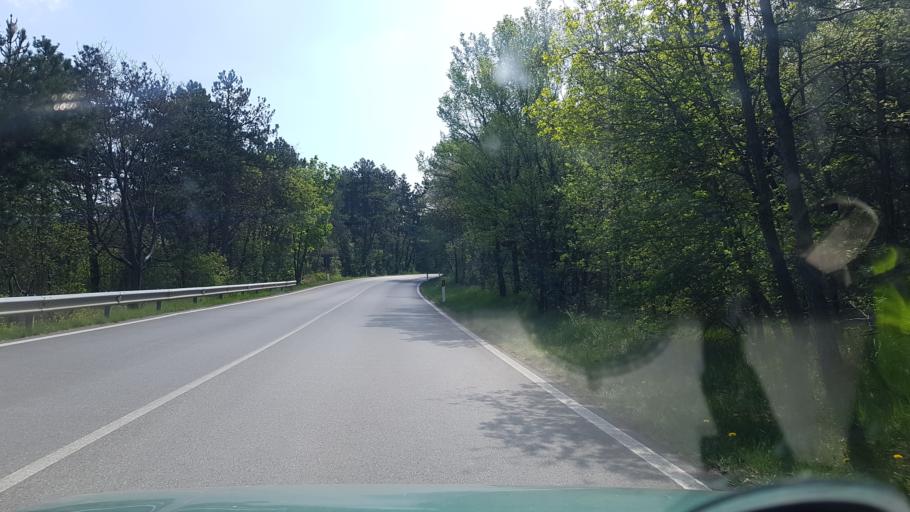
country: IT
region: Friuli Venezia Giulia
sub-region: Provincia di Trieste
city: Dolina
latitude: 45.6350
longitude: 13.8825
